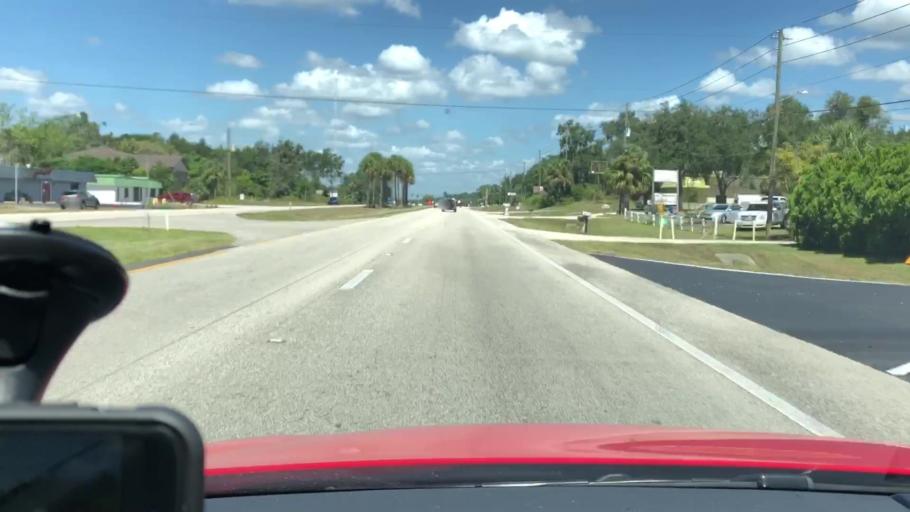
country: US
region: Florida
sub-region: Volusia County
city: Orange City
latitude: 28.9661
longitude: -81.2986
